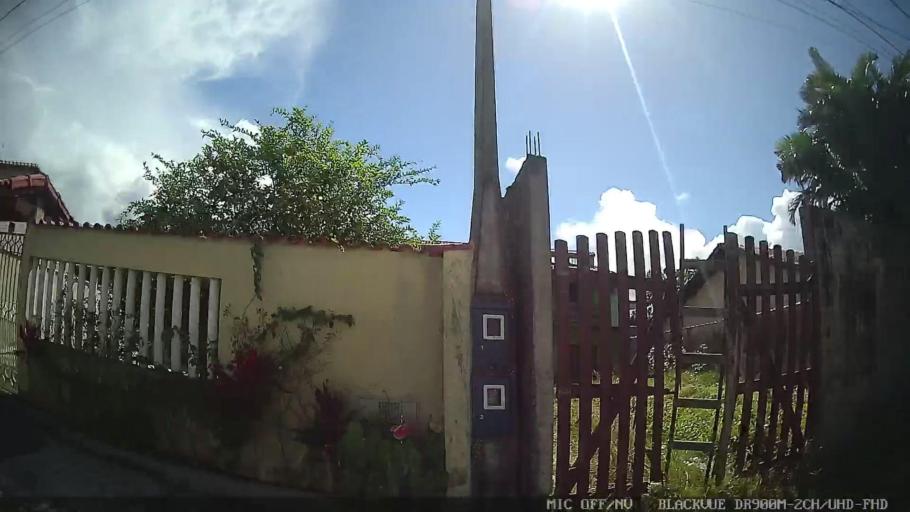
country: BR
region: Sao Paulo
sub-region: Itanhaem
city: Itanhaem
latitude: -24.2405
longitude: -46.8957
